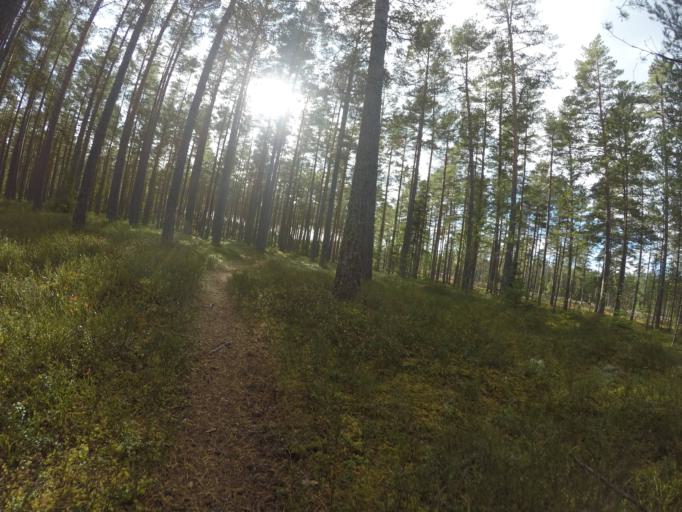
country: SE
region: Vaestmanland
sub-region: Kungsors Kommun
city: Kungsoer
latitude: 59.3227
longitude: 16.1129
